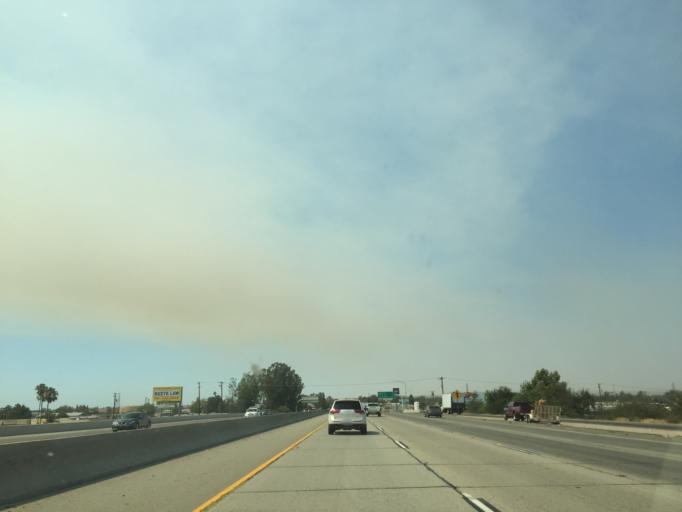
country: US
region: California
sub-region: Kern County
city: Bakersfield
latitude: 35.3872
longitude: -119.0445
